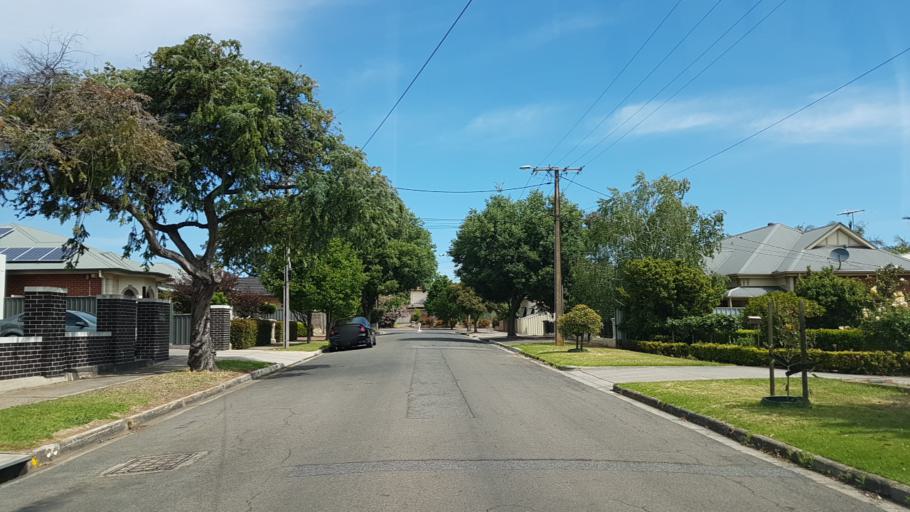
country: AU
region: South Australia
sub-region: Burnside
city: Kensington Gardens
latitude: -34.9127
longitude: 138.6650
